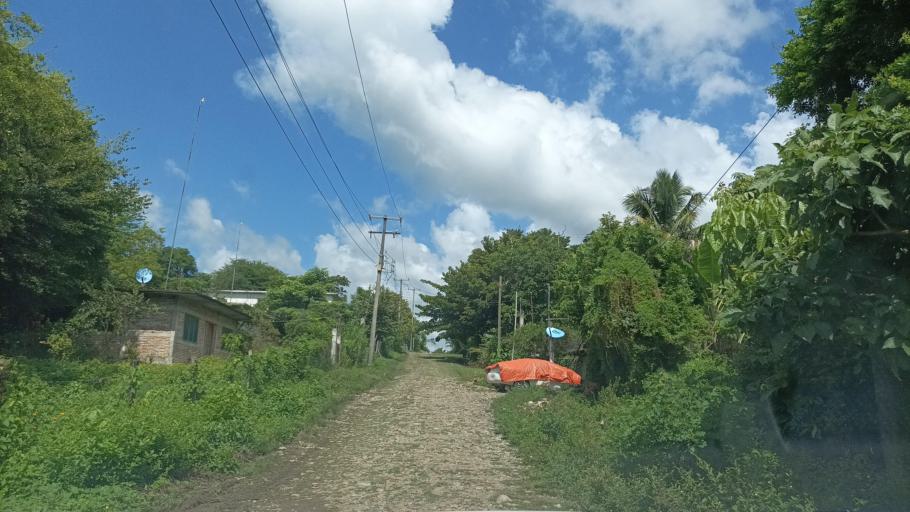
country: MX
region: Veracruz
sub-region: Tantoyuca
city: El Lindero
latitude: 21.1889
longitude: -98.1475
